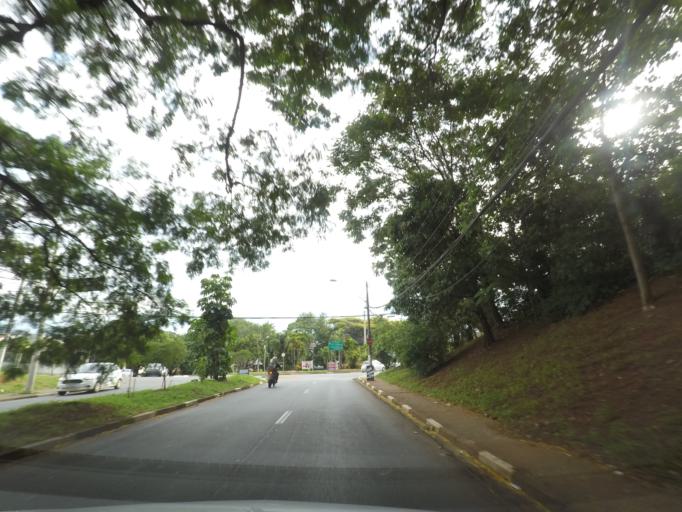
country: BR
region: Sao Paulo
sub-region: Campinas
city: Campinas
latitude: -22.8985
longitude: -47.0978
